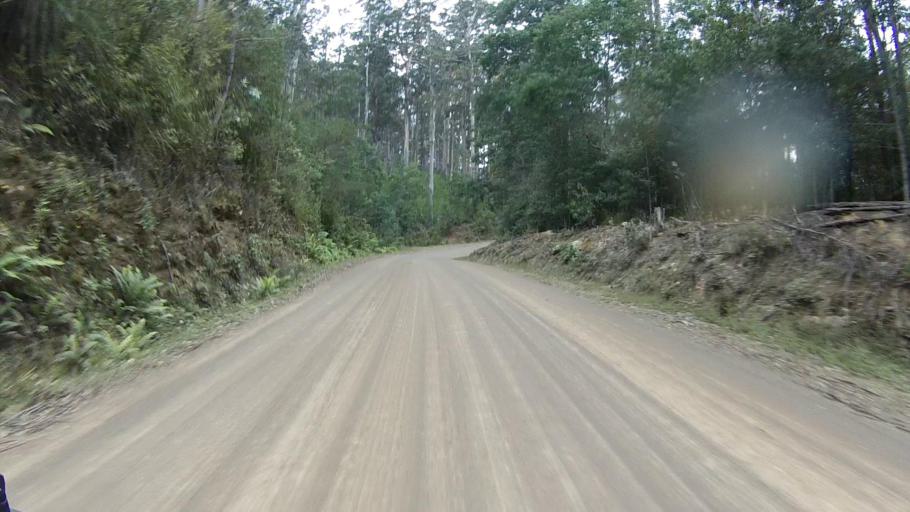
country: AU
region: Tasmania
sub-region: Sorell
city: Sorell
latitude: -42.7058
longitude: 147.8533
